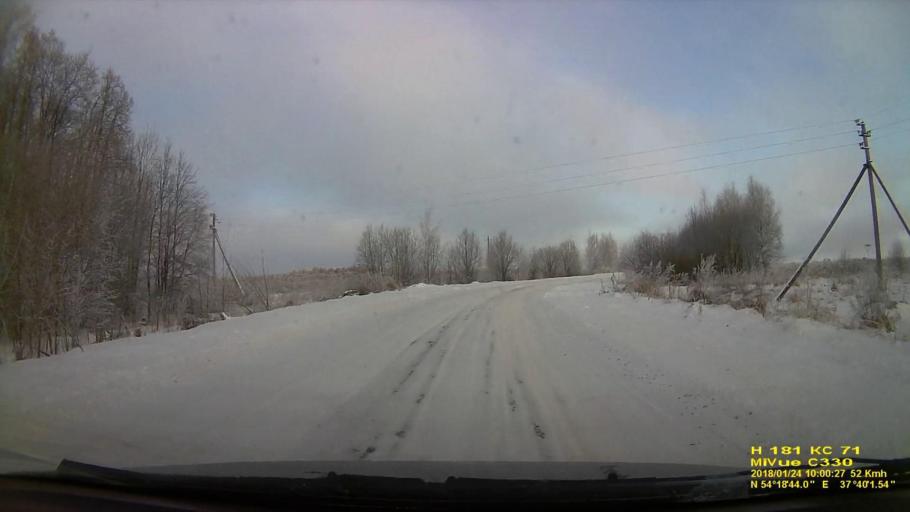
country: RU
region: Tula
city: Revyakino
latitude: 54.3122
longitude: 37.6671
